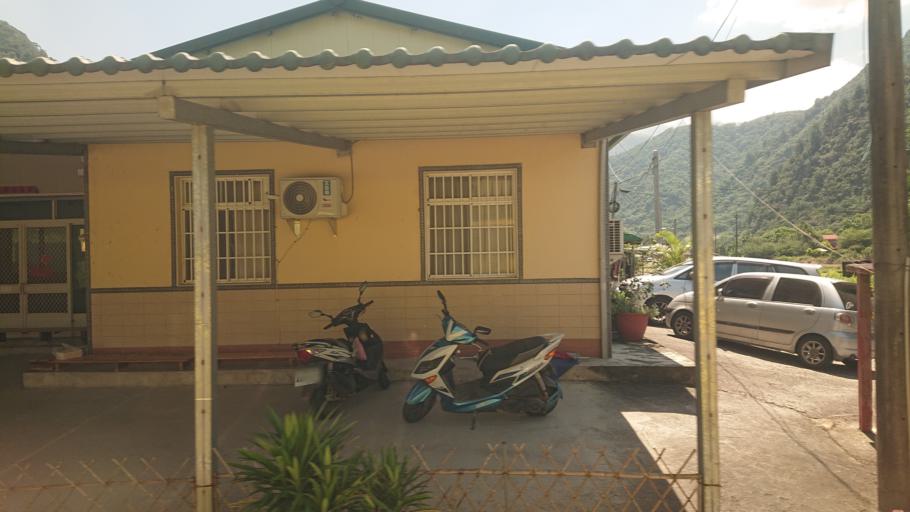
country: TW
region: Taiwan
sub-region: Nantou
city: Puli
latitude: 24.0665
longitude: 120.9531
